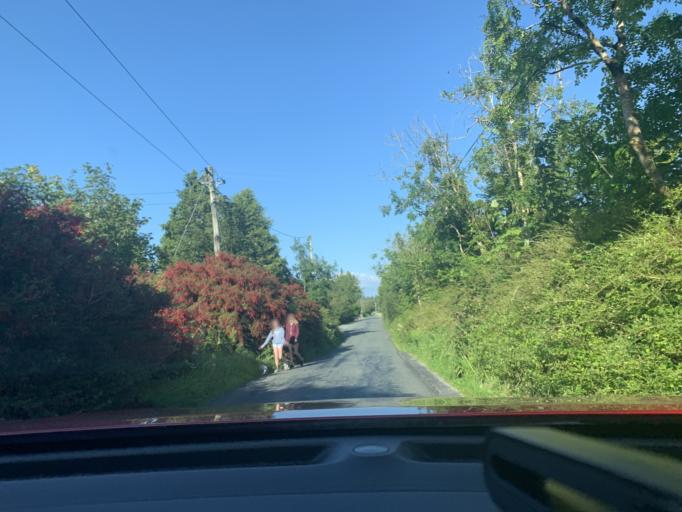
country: IE
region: Connaught
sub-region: Sligo
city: Tobercurry
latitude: 54.1199
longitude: -8.7531
